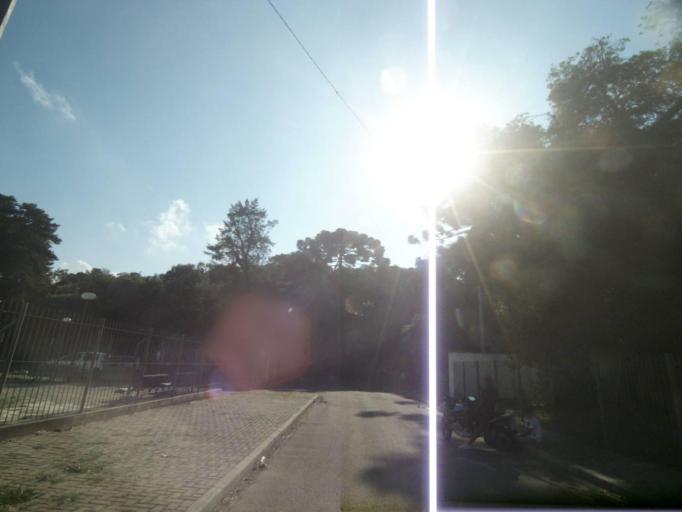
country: BR
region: Parana
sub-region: Araucaria
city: Araucaria
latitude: -25.5295
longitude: -49.3339
